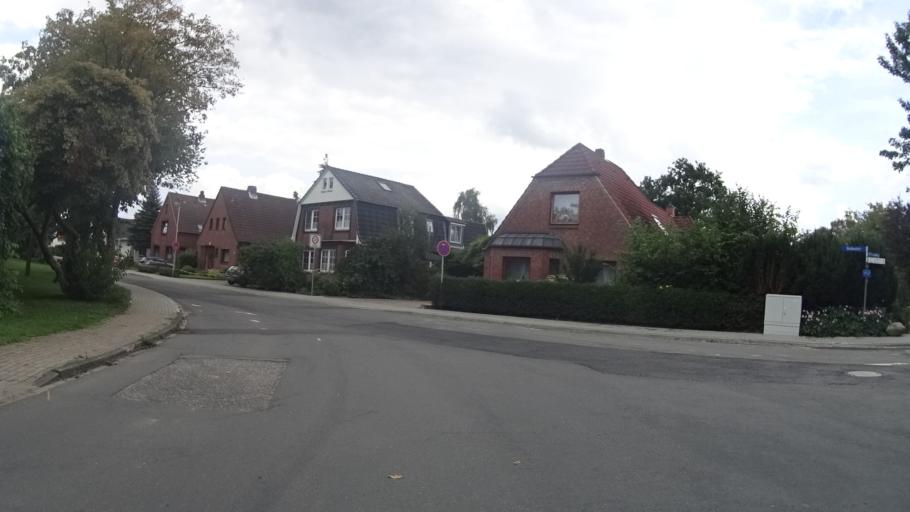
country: DE
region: Schleswig-Holstein
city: Gluckstadt
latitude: 53.7832
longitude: 9.4287
